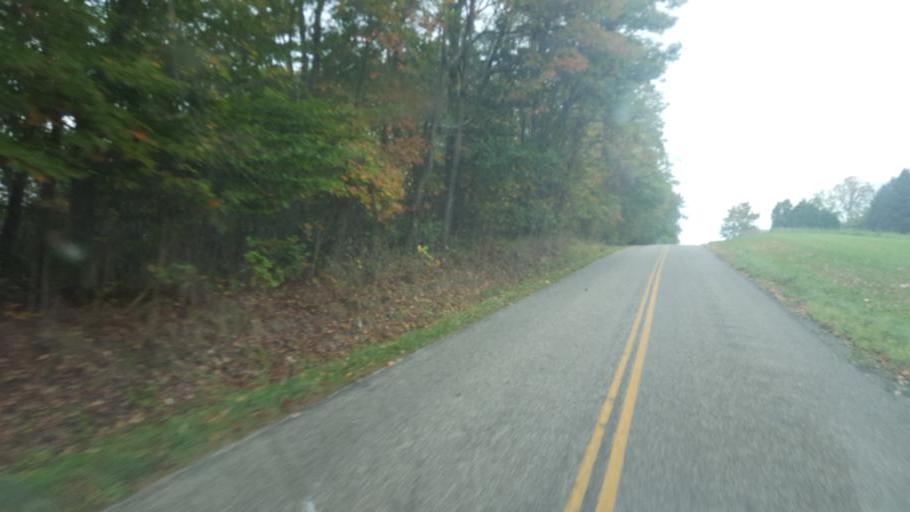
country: US
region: Ohio
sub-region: Carroll County
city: Carrollton
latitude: 40.5237
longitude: -81.1231
